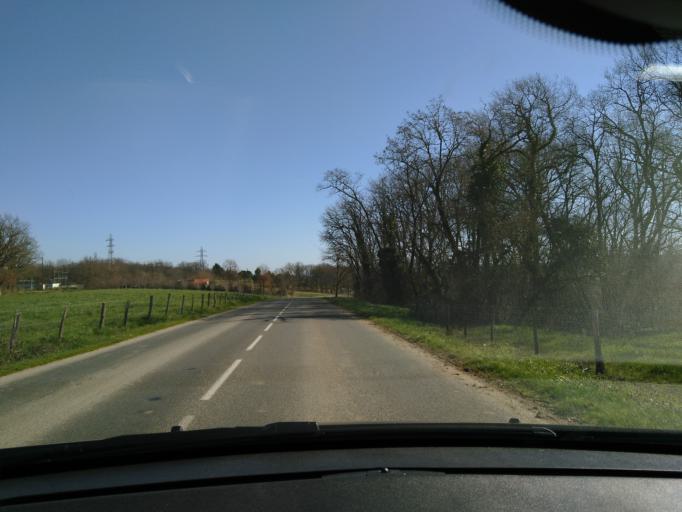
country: FR
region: Aquitaine
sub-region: Departement du Lot-et-Garonne
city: Cancon
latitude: 44.5358
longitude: 0.6432
